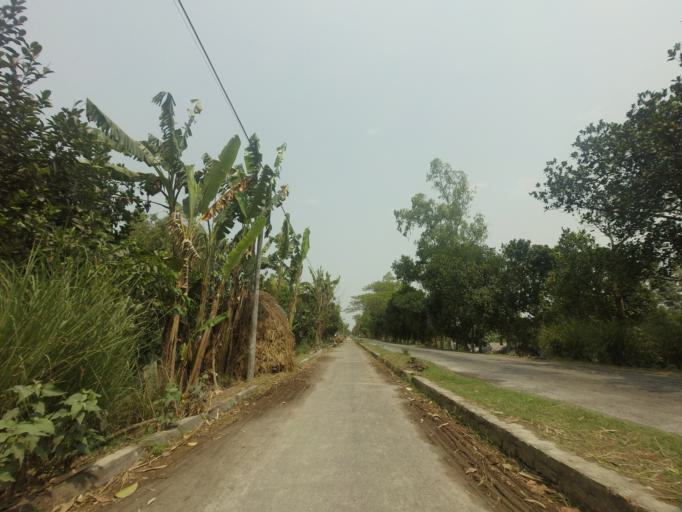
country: BD
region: Rajshahi
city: Sirajganj
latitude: 24.3501
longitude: 89.7021
